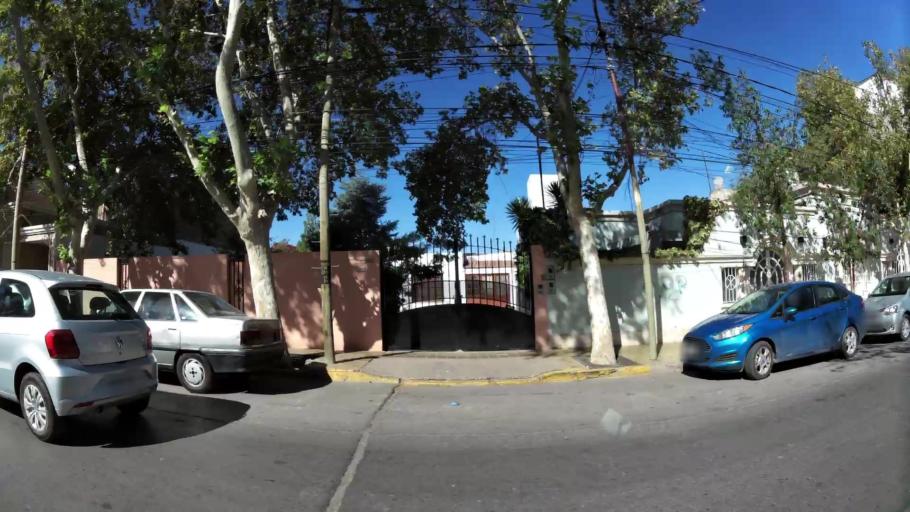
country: AR
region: San Juan
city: San Juan
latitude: -31.5369
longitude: -68.5350
